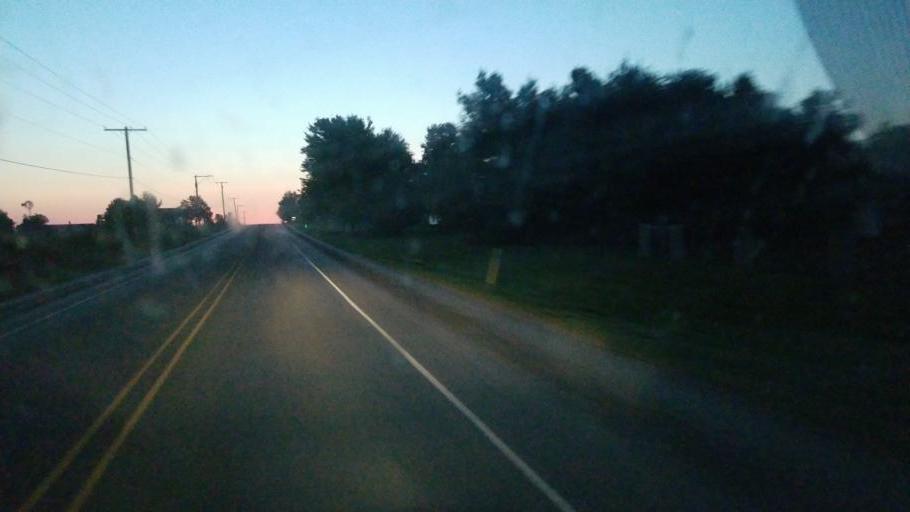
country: US
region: Indiana
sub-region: Elkhart County
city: Middlebury
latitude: 41.6757
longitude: -85.6611
